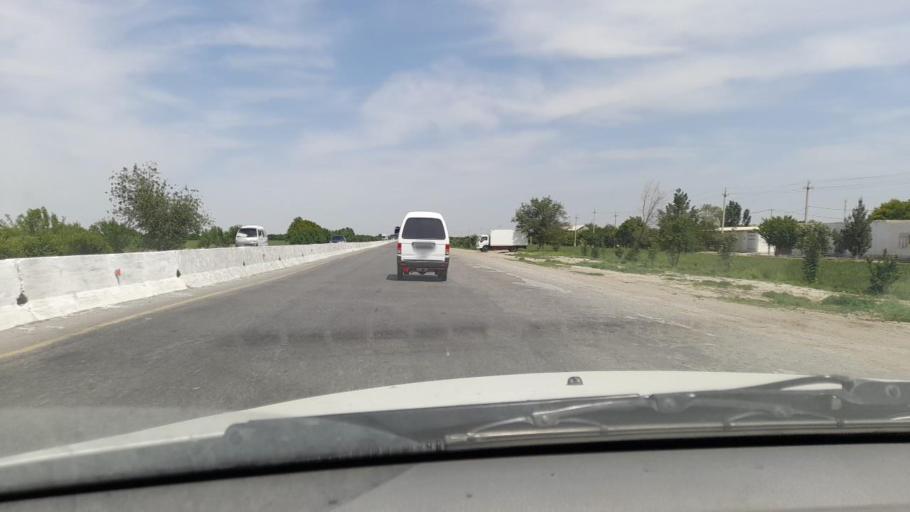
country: UZ
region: Bukhara
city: Wobkent
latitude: 40.0439
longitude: 64.5379
